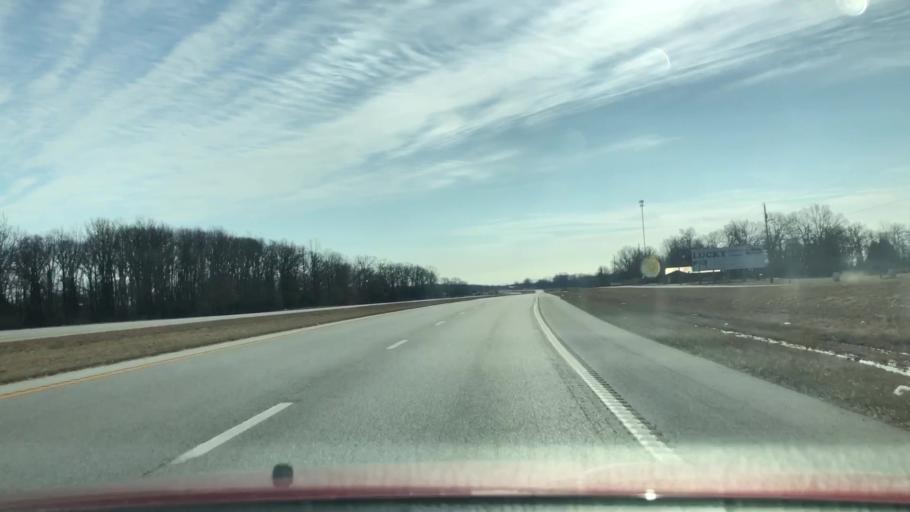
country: US
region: Missouri
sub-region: Webster County
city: Seymour
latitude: 37.1437
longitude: -92.7477
